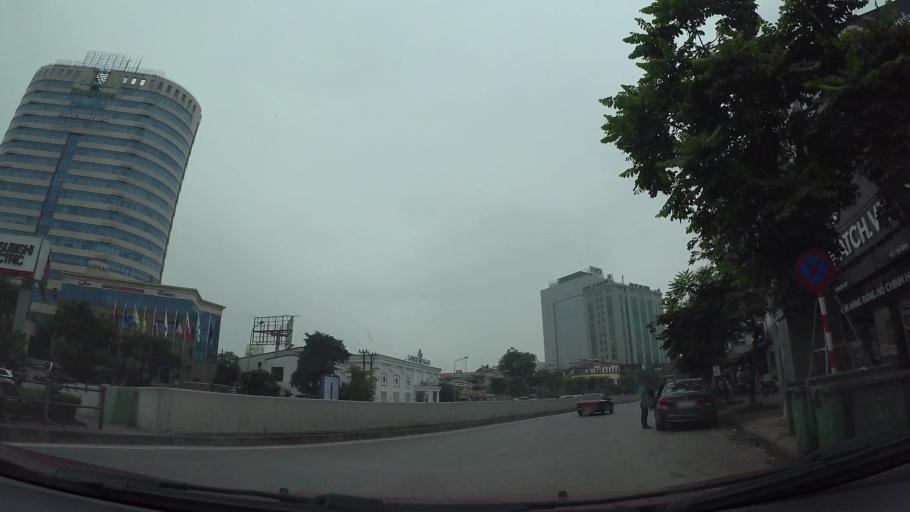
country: VN
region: Ha Noi
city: Hai BaTrung
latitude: 21.0080
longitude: 105.8407
